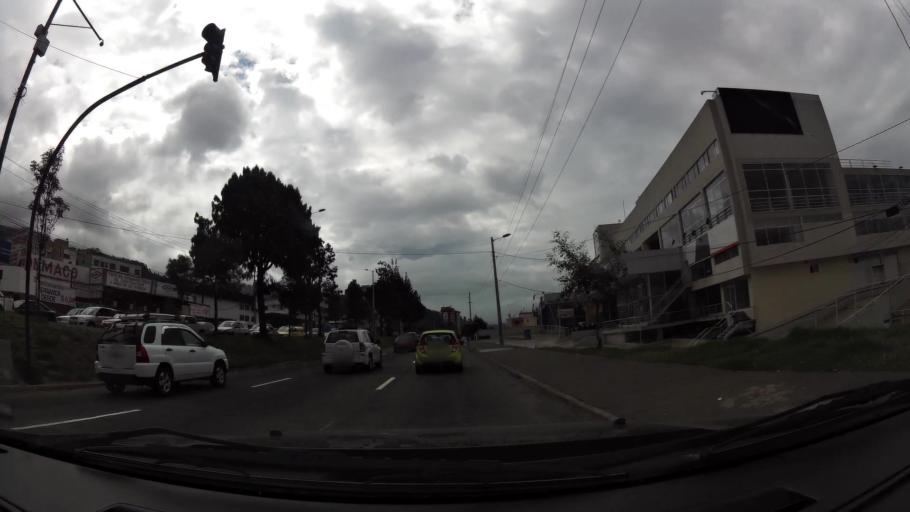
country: EC
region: Pichincha
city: Quito
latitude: -0.1444
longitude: -78.4998
